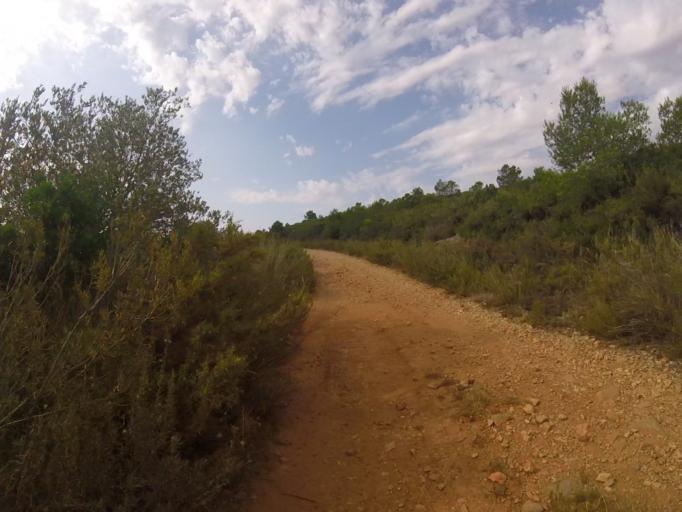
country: ES
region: Valencia
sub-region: Provincia de Castello
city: Alcala de Xivert
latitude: 40.3860
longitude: 0.2116
